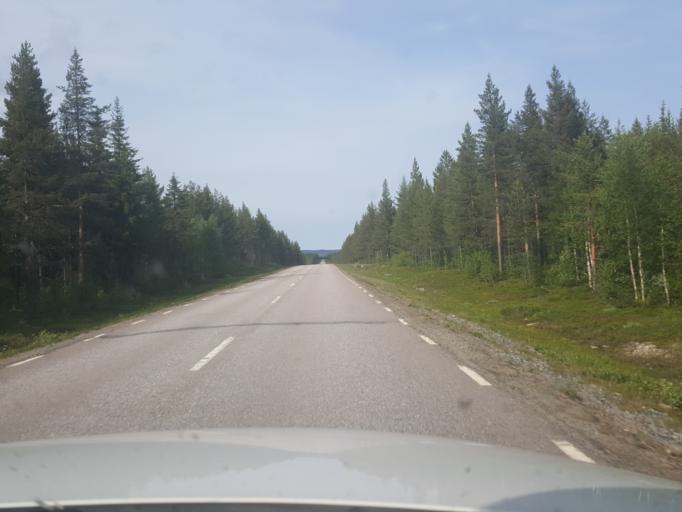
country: SE
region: Norrbotten
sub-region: Arjeplogs Kommun
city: Arjeplog
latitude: 65.6976
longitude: 18.0711
